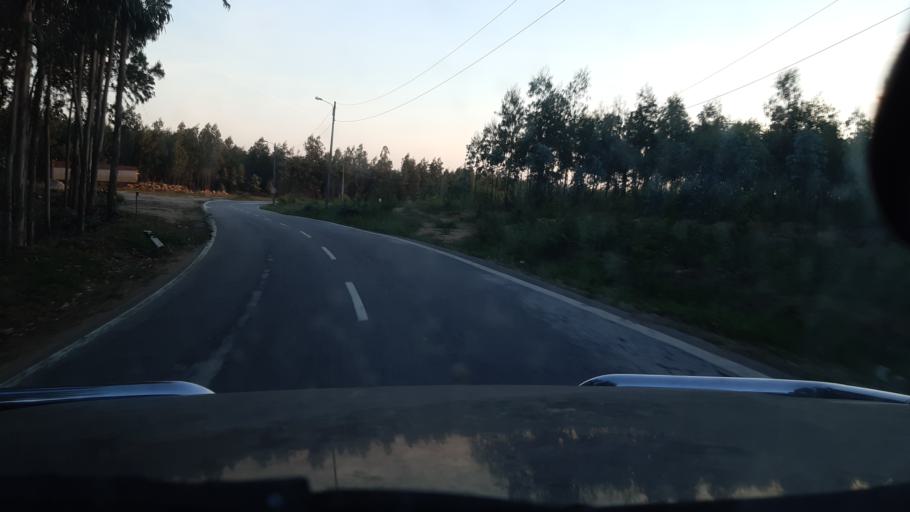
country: PT
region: Aveiro
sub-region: Agueda
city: Aguada de Cima
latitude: 40.5665
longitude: -8.3710
